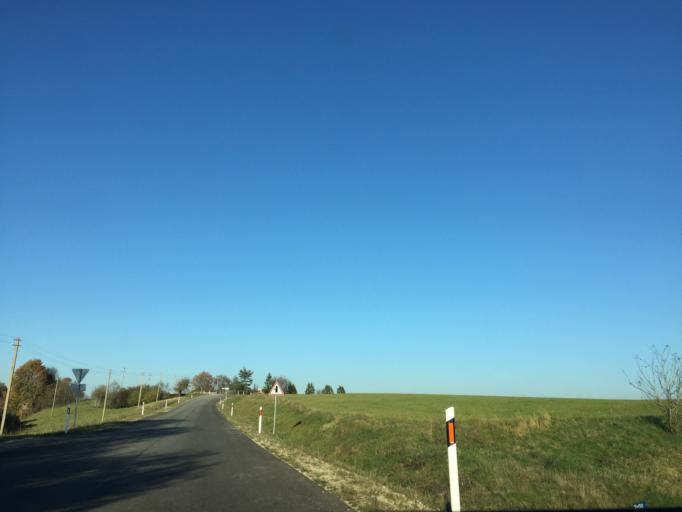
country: LT
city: Plateliai
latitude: 56.0686
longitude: 21.8559
